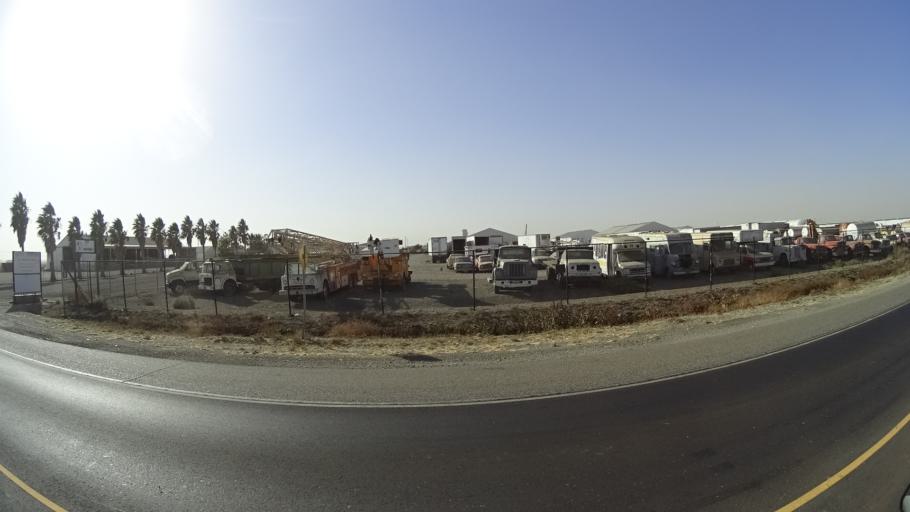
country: US
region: California
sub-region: Yolo County
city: Woodland
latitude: 38.7497
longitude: -121.7293
